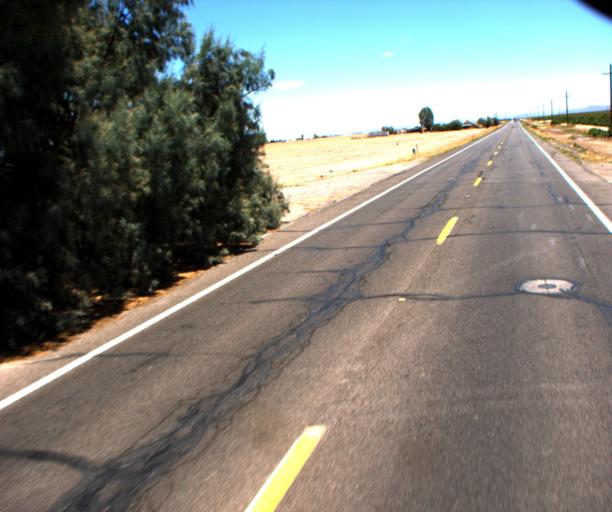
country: US
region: Arizona
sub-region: Pinal County
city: Casa Grande
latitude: 32.8797
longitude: -111.6279
